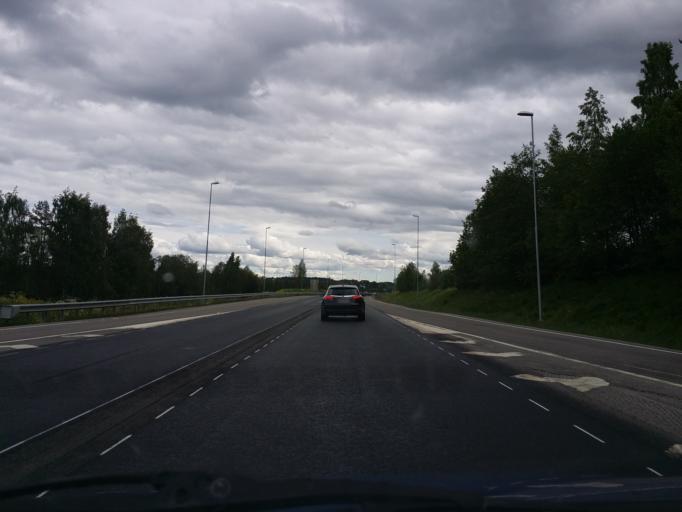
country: NO
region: Hedmark
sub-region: Hamar
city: Hamar
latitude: 60.8328
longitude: 11.0803
